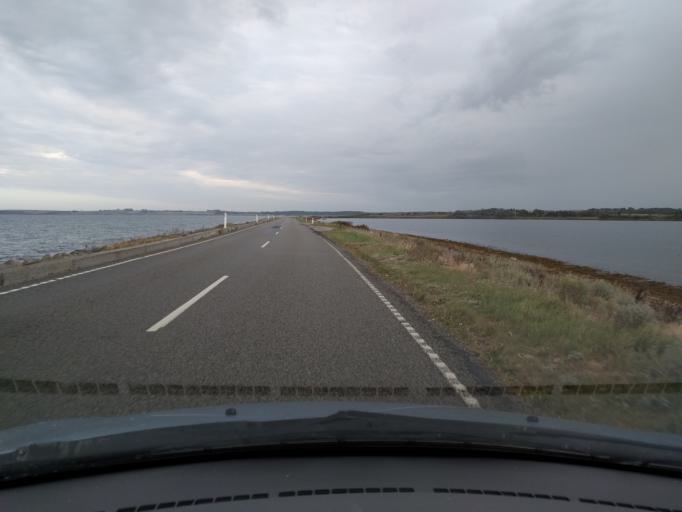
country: DK
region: South Denmark
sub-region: Assens Kommune
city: Assens
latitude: 55.1817
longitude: 9.9854
